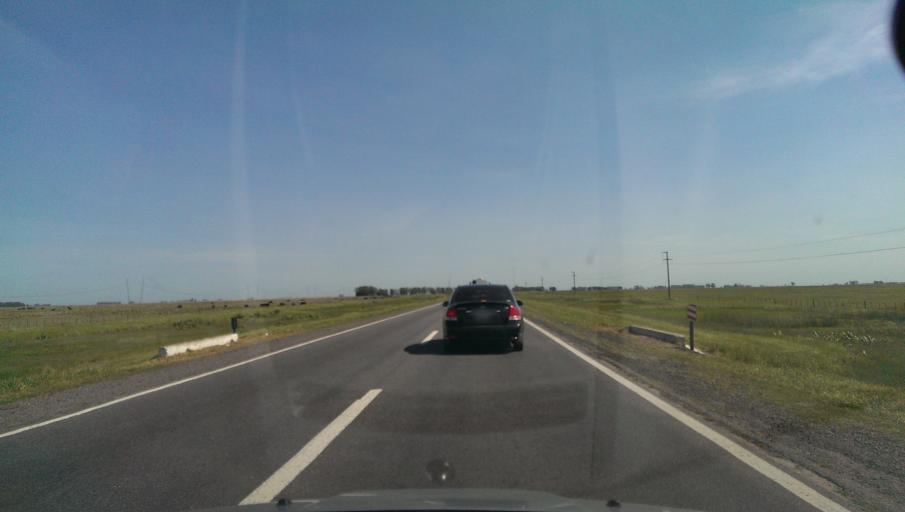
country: AR
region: Buenos Aires
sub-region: Partido de Azul
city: Azul
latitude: -36.5915
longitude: -59.6549
